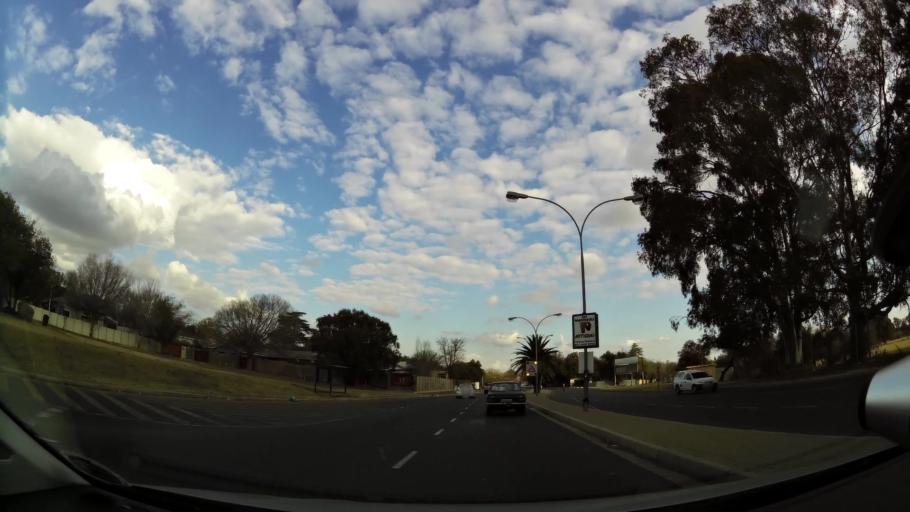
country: ZA
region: Orange Free State
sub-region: Mangaung Metropolitan Municipality
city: Bloemfontein
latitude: -29.0969
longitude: 26.2033
